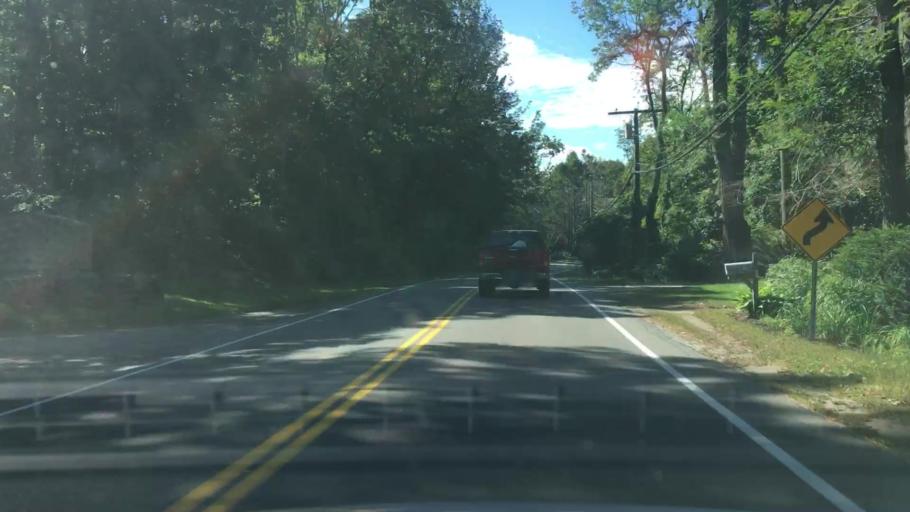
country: US
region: Maine
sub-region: York County
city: Kittery Point
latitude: 43.0827
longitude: -70.7105
